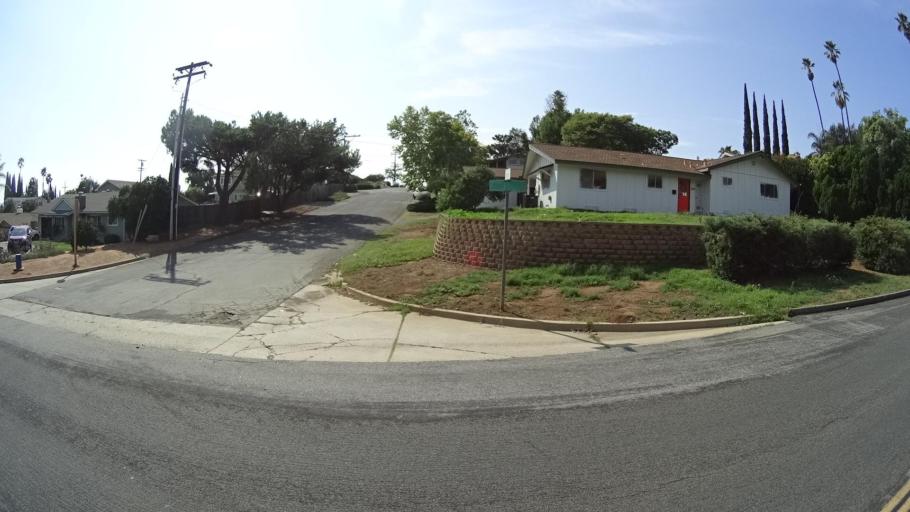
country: US
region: California
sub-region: San Diego County
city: Escondido
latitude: 33.1007
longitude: -117.0654
